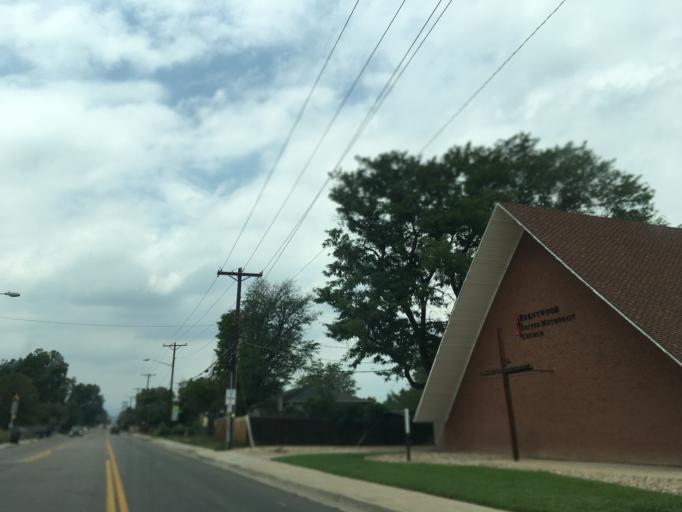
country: US
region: Colorado
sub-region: Arapahoe County
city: Sheridan
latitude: 39.6822
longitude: -105.0298
